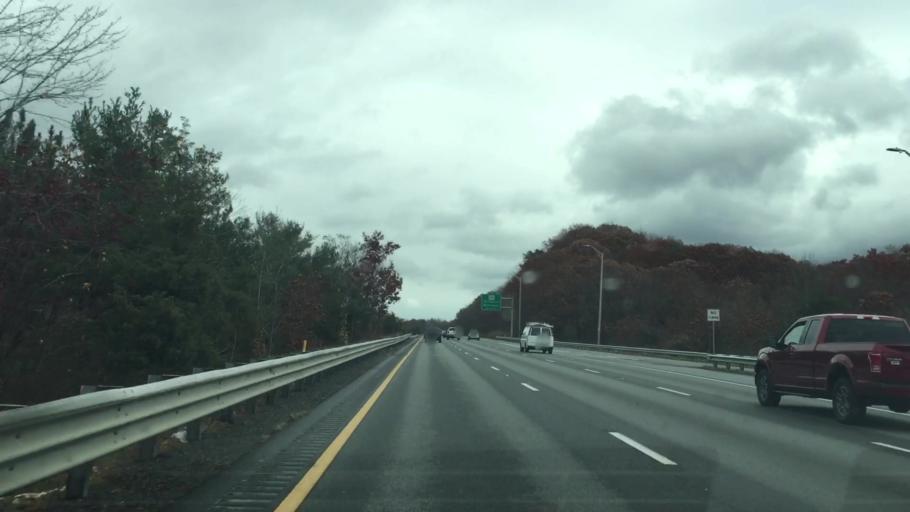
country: US
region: Massachusetts
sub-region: Essex County
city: Haverhill
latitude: 42.8038
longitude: -71.0606
